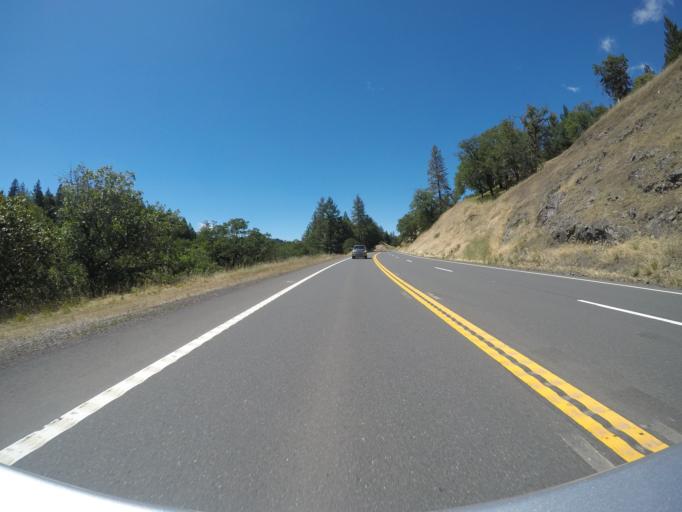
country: US
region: California
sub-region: Mendocino County
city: Laytonville
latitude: 39.7512
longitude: -123.5348
